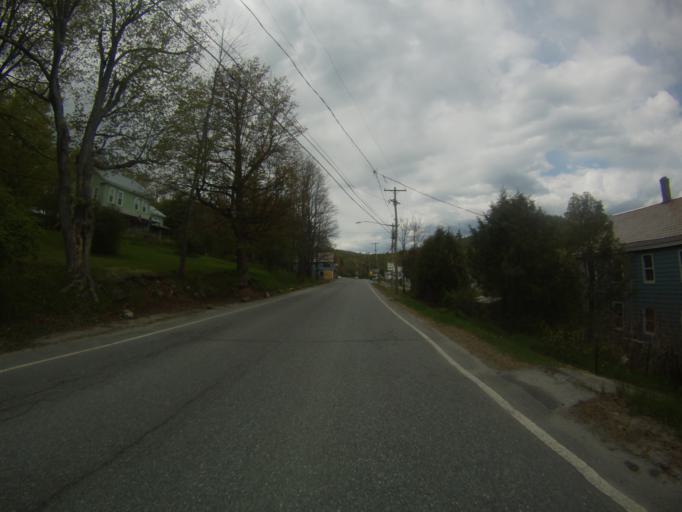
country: US
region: New York
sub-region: Essex County
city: Mineville
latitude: 44.0858
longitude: -73.5316
